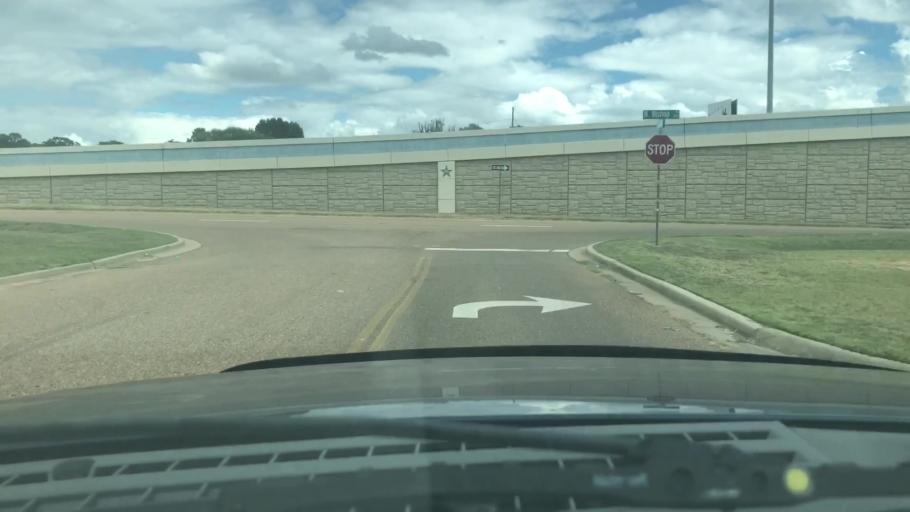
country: US
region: Texas
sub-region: Bowie County
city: Wake Village
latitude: 33.4482
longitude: -94.0977
